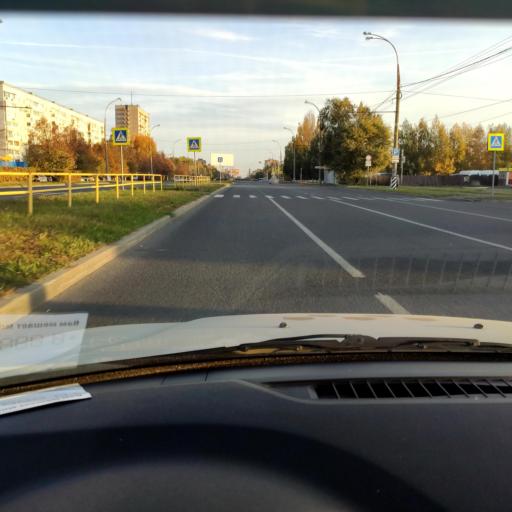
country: RU
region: Samara
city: Tol'yatti
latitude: 53.5014
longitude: 49.2906
